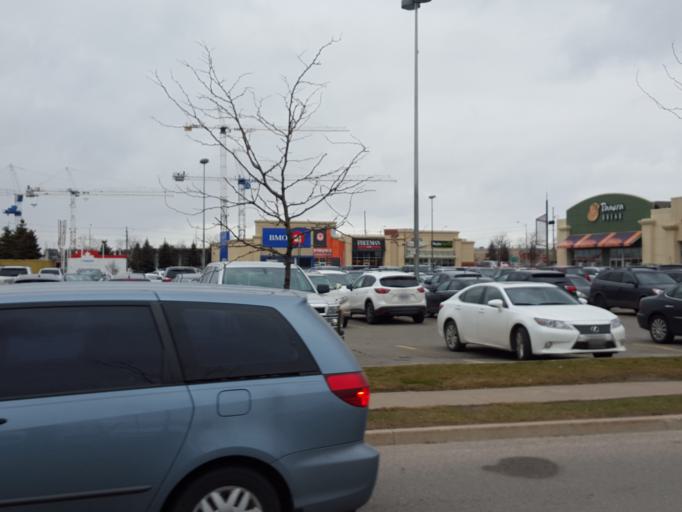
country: CA
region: Ontario
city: Concord
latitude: 43.7876
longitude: -79.5458
